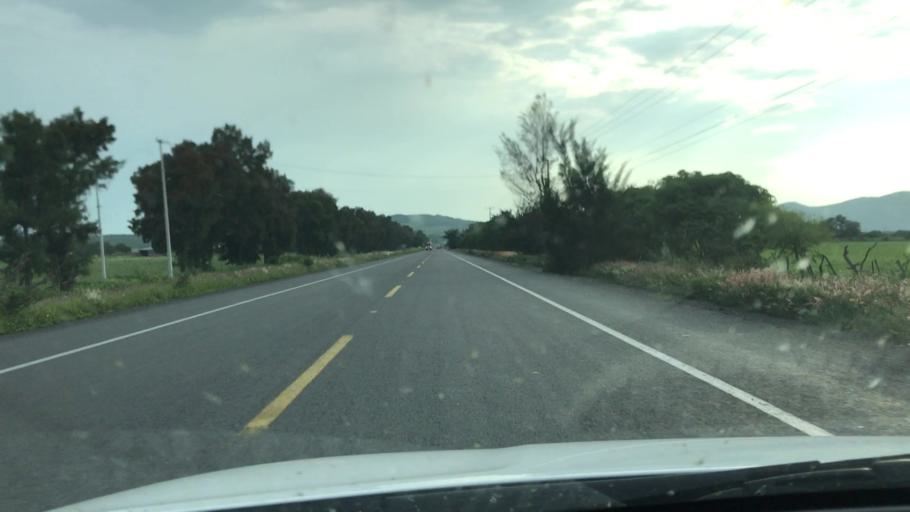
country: MX
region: Michoacan
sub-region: Yurecuaro
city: Yurecuaro
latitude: 20.3415
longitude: -102.1681
